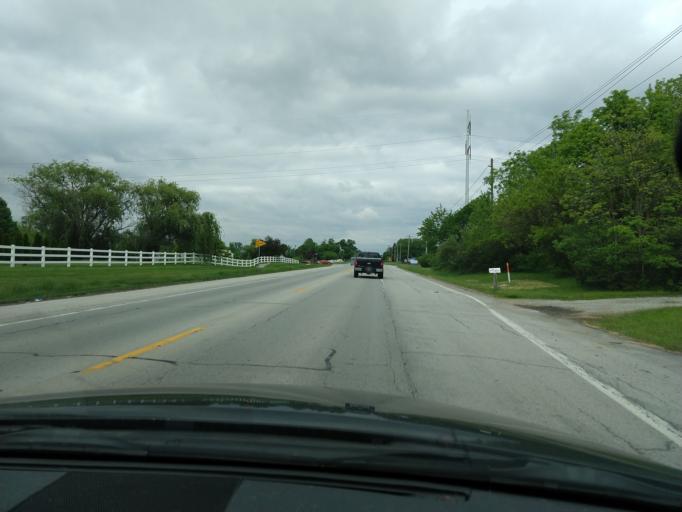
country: US
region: Indiana
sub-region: Hamilton County
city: Westfield
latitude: 40.0429
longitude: -86.0963
